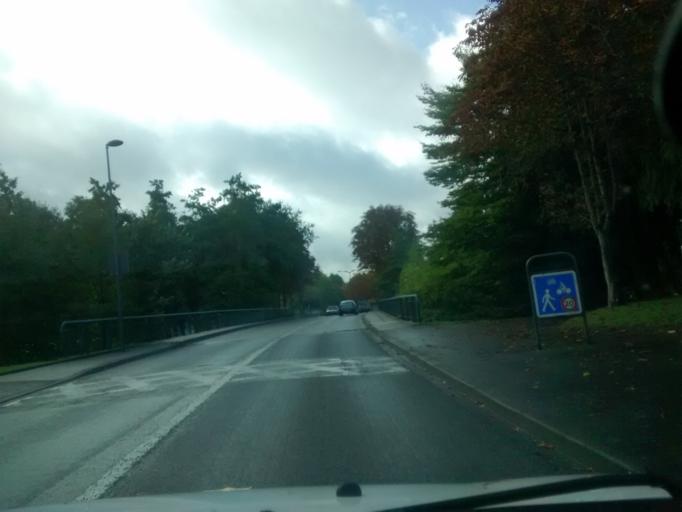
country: FR
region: Brittany
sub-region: Departement d'Ille-et-Vilaine
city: Cesson-Sevigne
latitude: 48.1175
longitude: -1.6006
